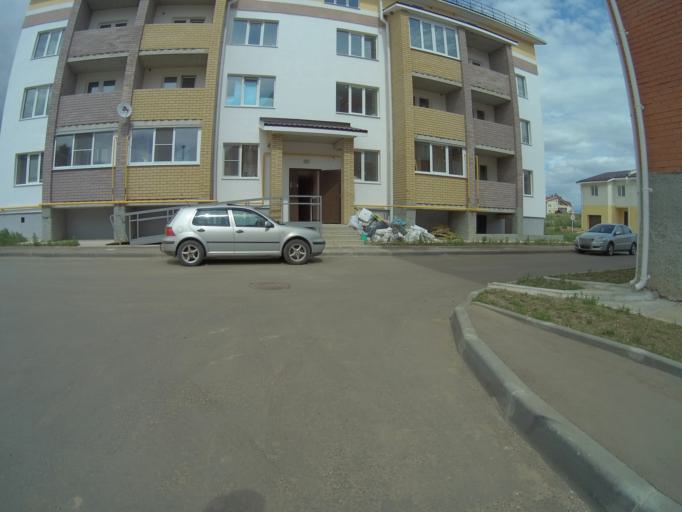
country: RU
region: Vladimir
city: Bogolyubovo
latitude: 56.1996
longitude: 40.5243
